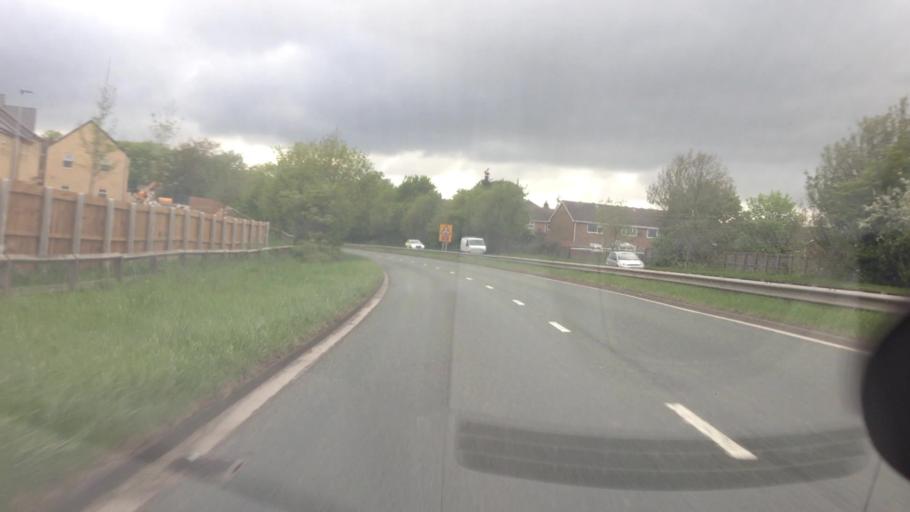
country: GB
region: England
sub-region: City and Borough of Wakefield
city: Ossett
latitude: 53.6937
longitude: -1.5832
